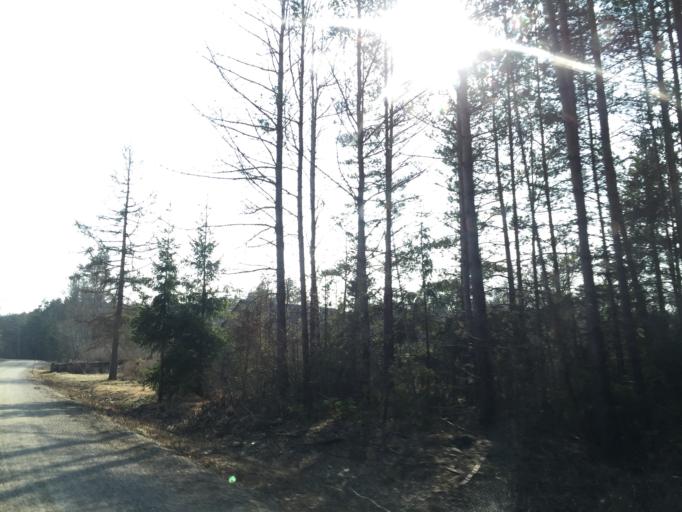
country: EE
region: Saare
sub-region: Orissaare vald
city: Orissaare
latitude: 58.5663
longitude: 23.2729
